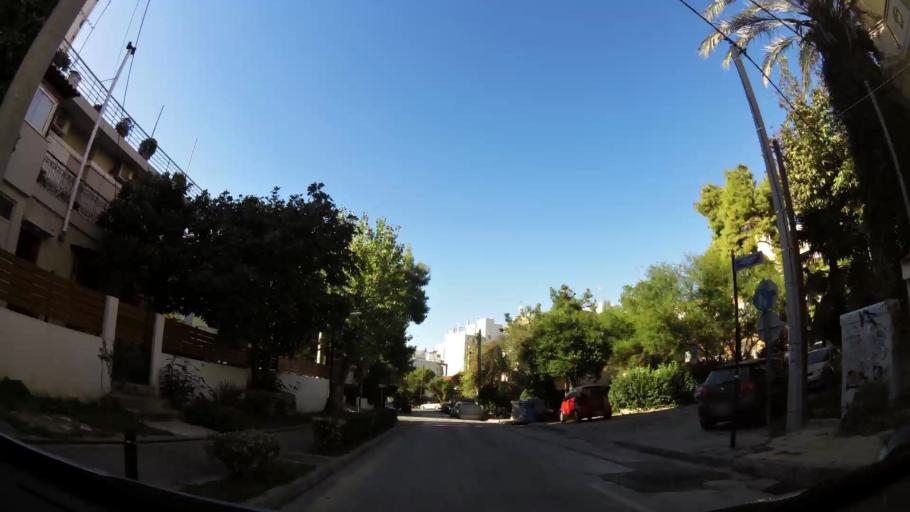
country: GR
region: Attica
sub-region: Nomarchia Athinas
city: Nea Erythraia
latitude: 38.0921
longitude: 23.8171
